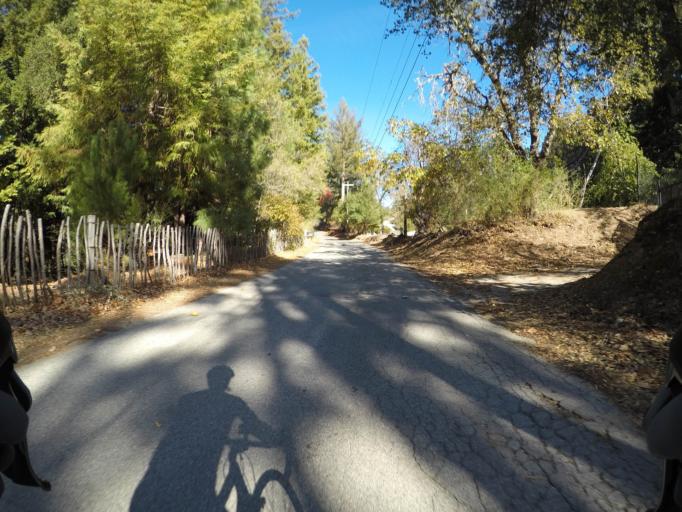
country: US
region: California
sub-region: Santa Clara County
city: Lexington Hills
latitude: 37.1221
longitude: -121.9898
